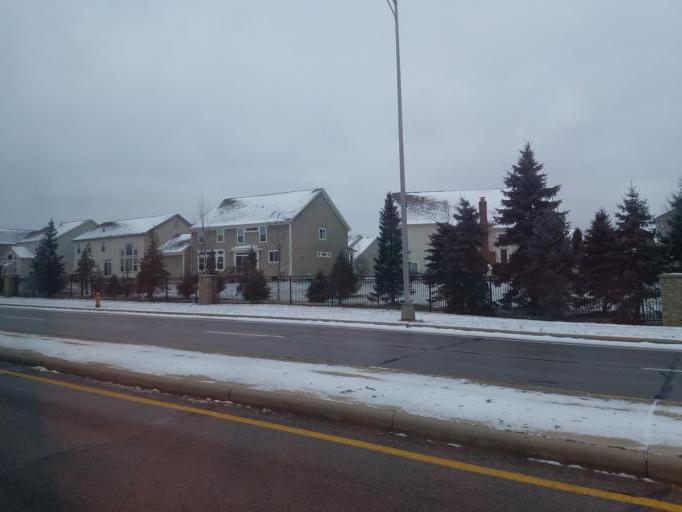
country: US
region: Ohio
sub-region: Franklin County
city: Worthington
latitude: 40.1166
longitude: -83.0454
